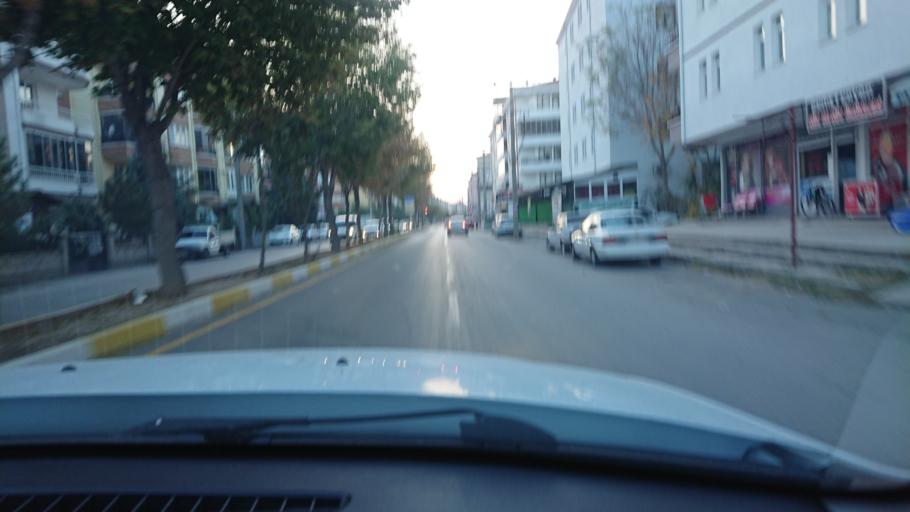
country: TR
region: Aksaray
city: Aksaray
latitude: 38.3608
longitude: 34.0223
